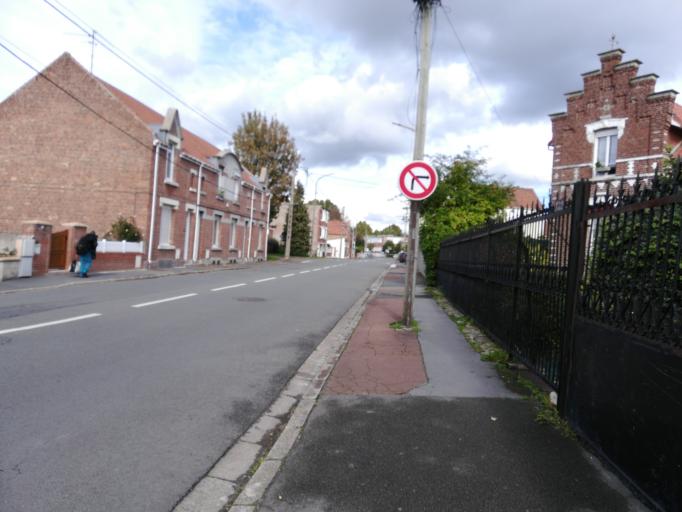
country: FR
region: Nord-Pas-de-Calais
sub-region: Departement du Pas-de-Calais
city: Montigny-en-Gohelle
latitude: 50.4284
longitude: 2.9451
